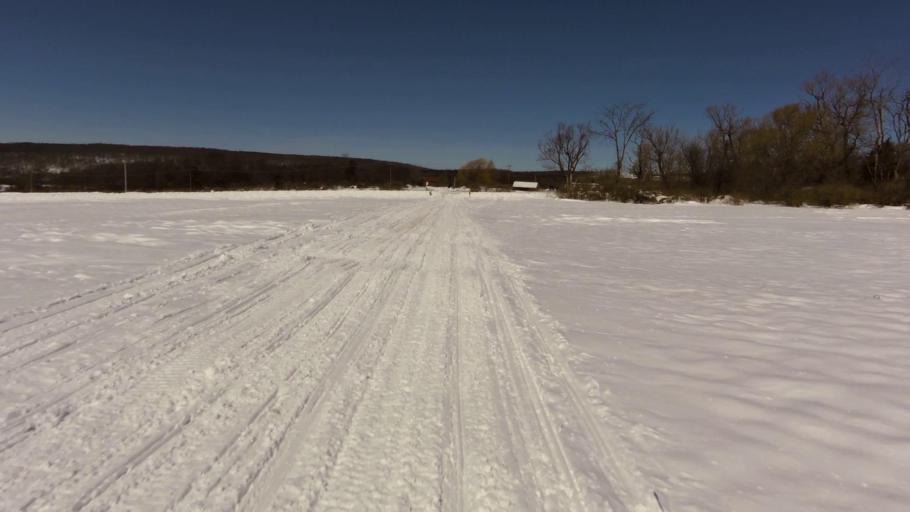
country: US
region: New York
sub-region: Wyoming County
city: Arcade
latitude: 42.4345
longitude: -78.3089
